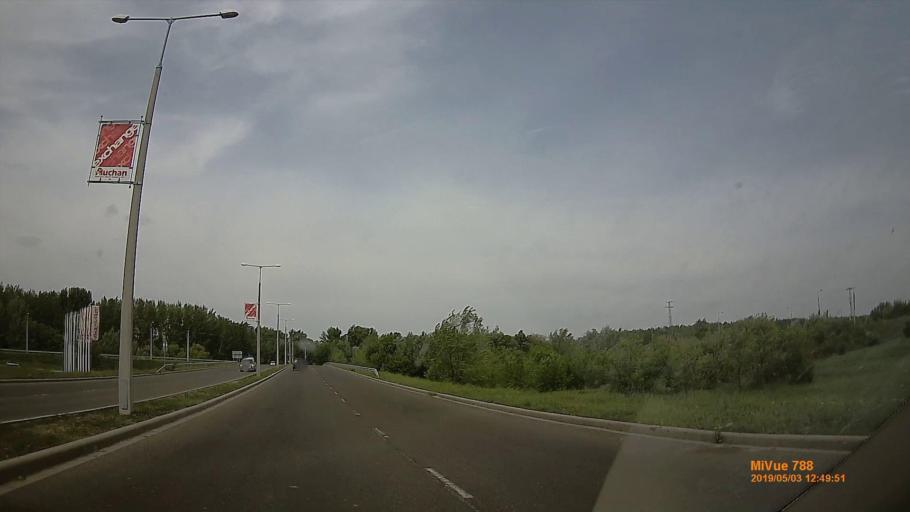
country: HU
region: Jasz-Nagykun-Szolnok
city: Szolnok
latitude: 47.1619
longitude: 20.2010
